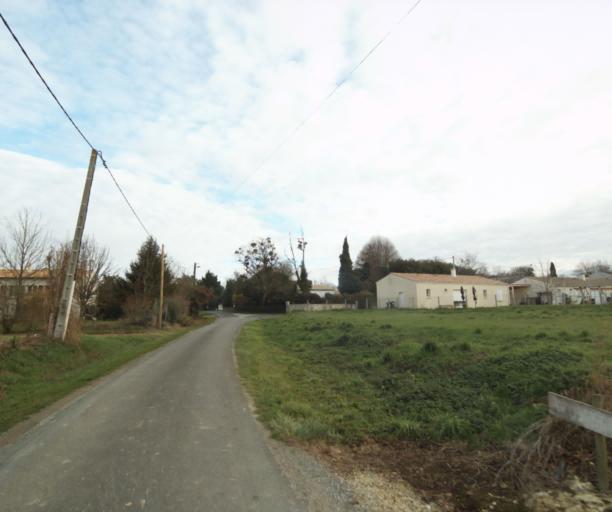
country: FR
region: Poitou-Charentes
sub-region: Departement de la Charente-Maritime
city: Corme-Royal
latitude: 45.7450
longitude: -0.8011
